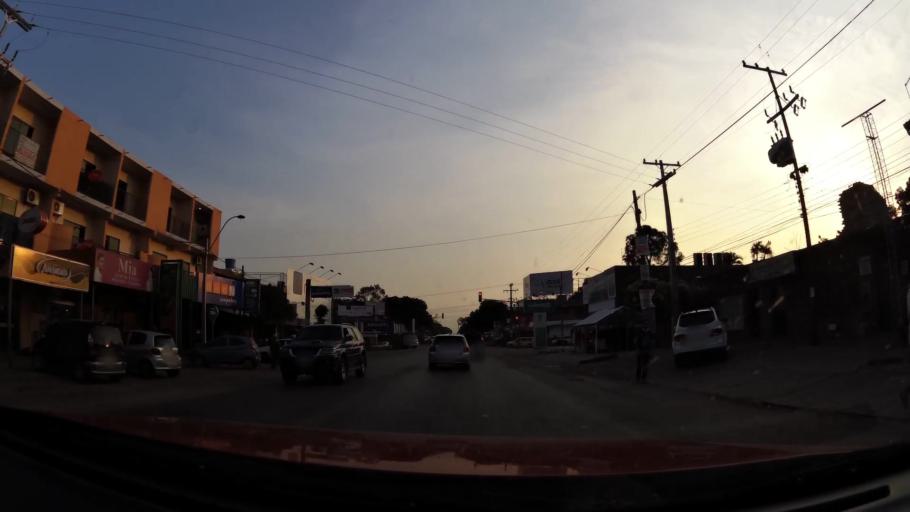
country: PY
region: Central
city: Villa Elisa
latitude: -25.3573
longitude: -57.5954
